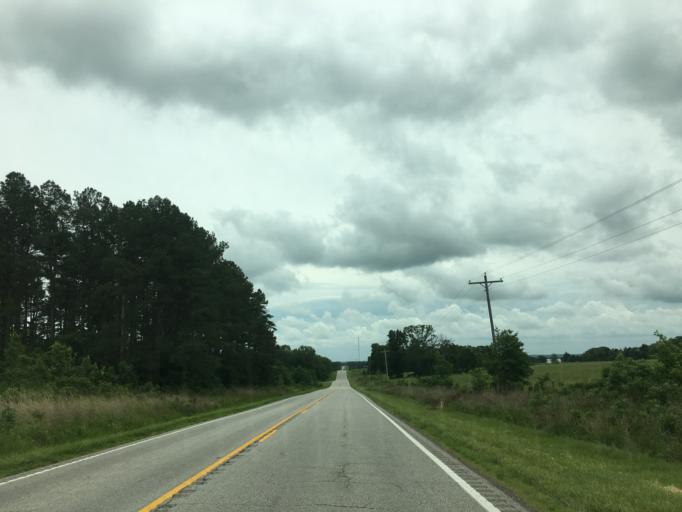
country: US
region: Missouri
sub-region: Gasconade County
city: Owensville
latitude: 38.5066
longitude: -91.4619
